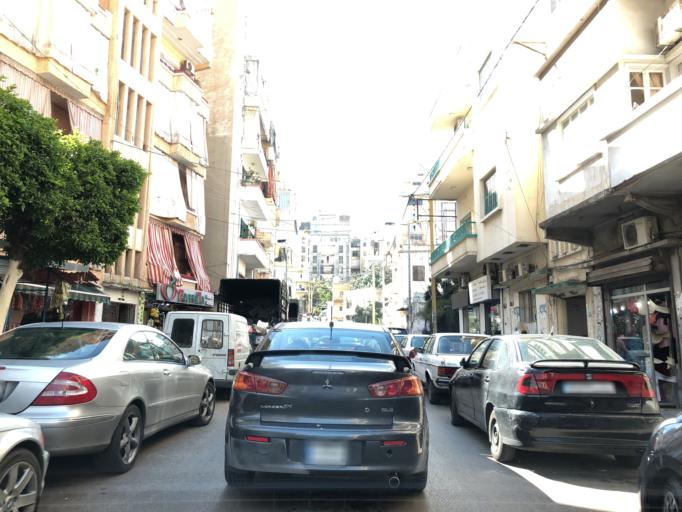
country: LB
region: Beyrouth
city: Beirut
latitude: 33.8886
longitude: 35.5275
